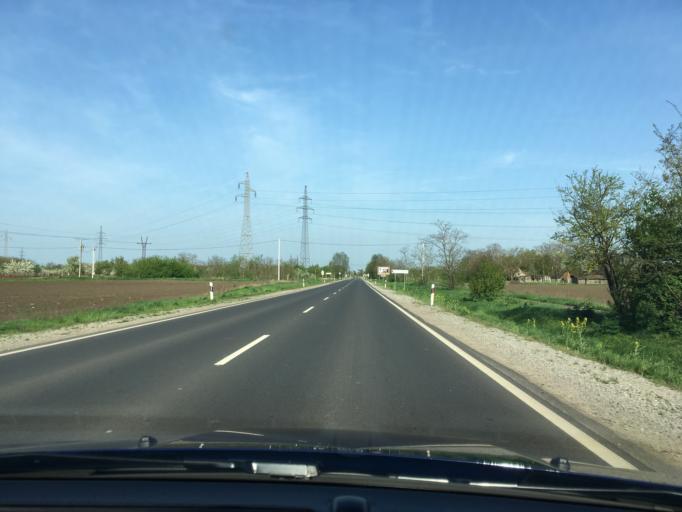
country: HU
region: Bekes
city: Bekescsaba
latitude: 46.6791
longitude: 21.0362
